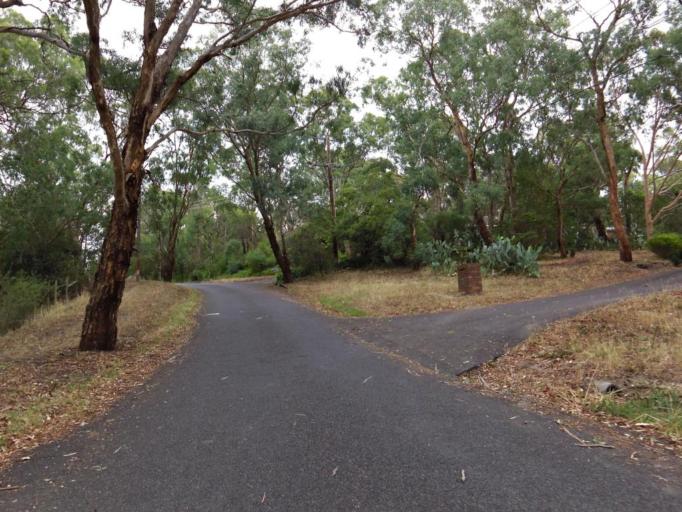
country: AU
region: Victoria
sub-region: Manningham
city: Templestowe Lower
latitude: -37.7641
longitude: 145.1272
